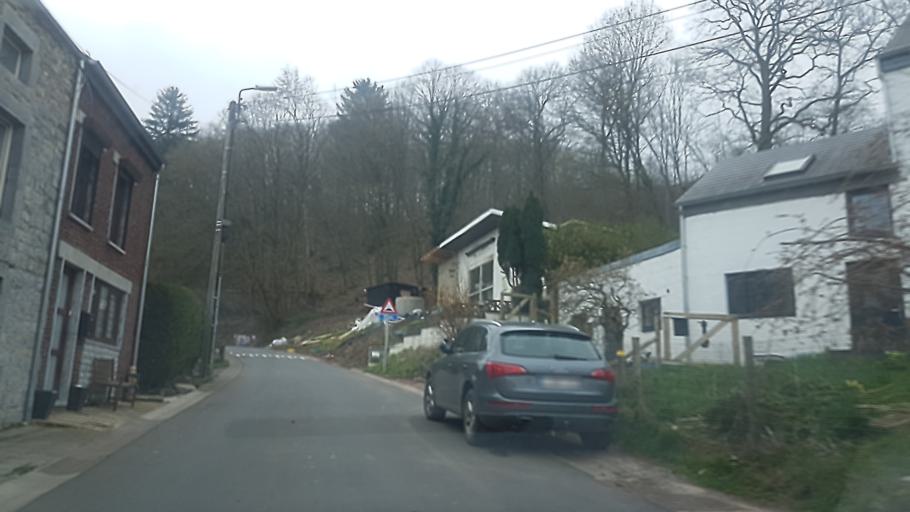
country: FR
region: Champagne-Ardenne
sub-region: Departement des Ardennes
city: Vireux-Molhain
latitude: 50.0772
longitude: 4.6356
